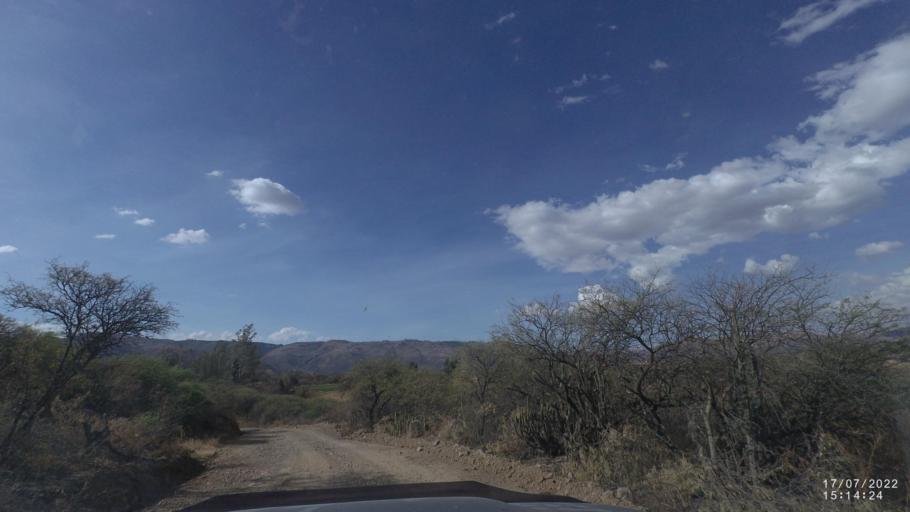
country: BO
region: Cochabamba
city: Capinota
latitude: -17.5625
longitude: -66.2617
